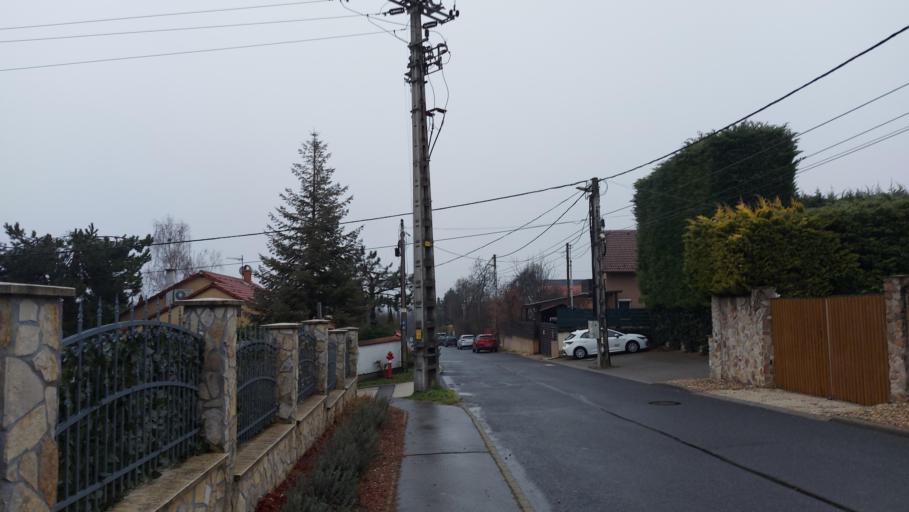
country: HU
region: Pest
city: Budaors
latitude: 47.4556
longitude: 18.9292
